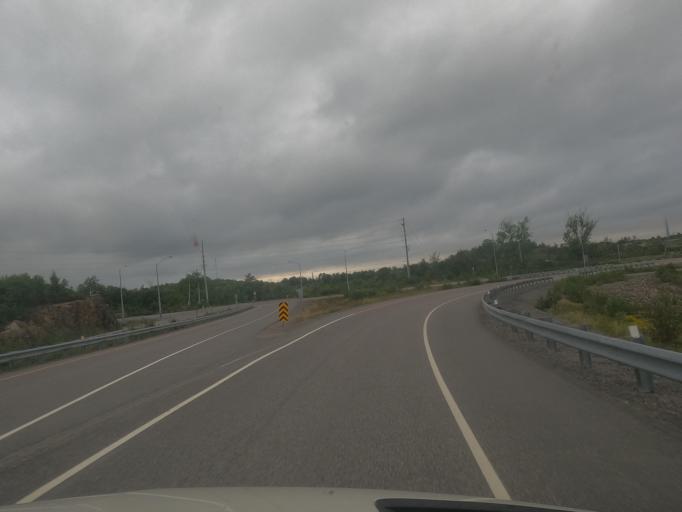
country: CA
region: Ontario
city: Greater Sudbury
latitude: 46.4302
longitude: -81.0079
